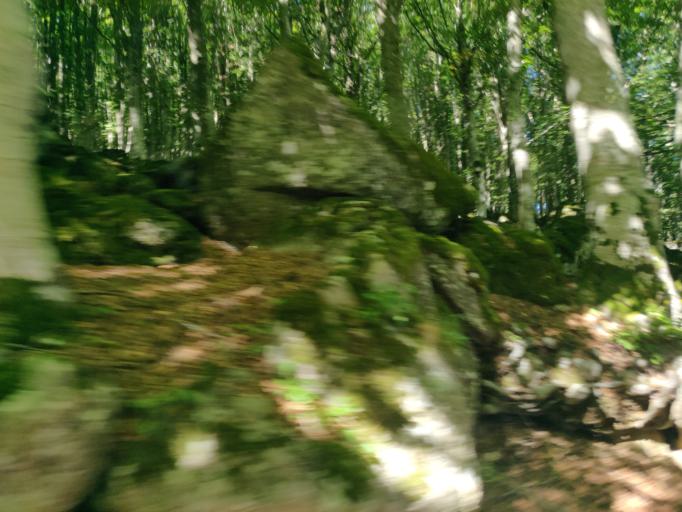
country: IT
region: Tuscany
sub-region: Provincia di Siena
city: Abbadia San Salvatore
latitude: 42.8935
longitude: 11.6327
